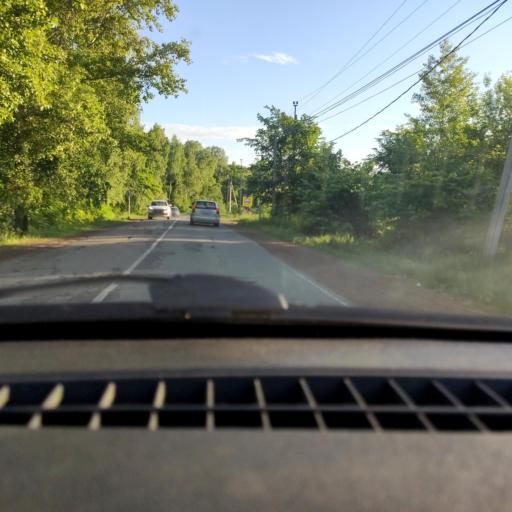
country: RU
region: Bashkortostan
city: Avdon
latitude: 54.6401
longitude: 55.7010
